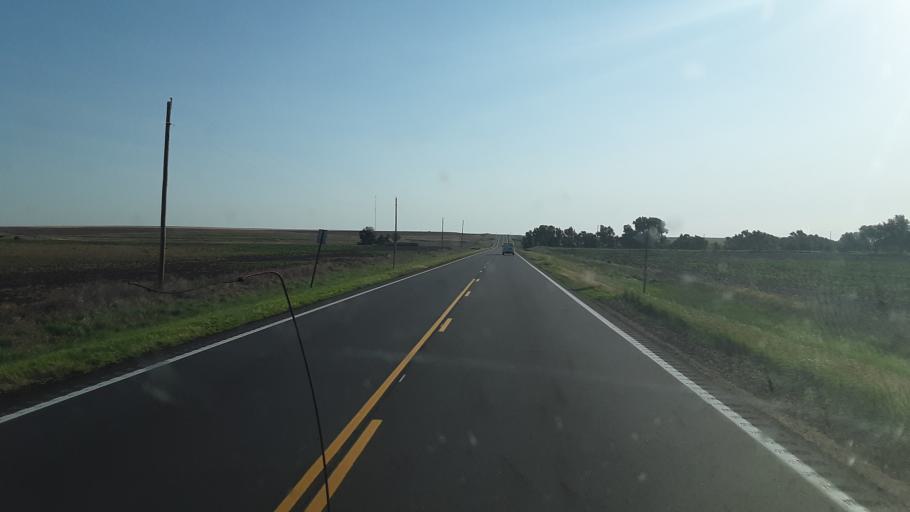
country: US
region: Kansas
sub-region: Hodgeman County
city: Jetmore
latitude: 38.0749
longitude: -99.9883
